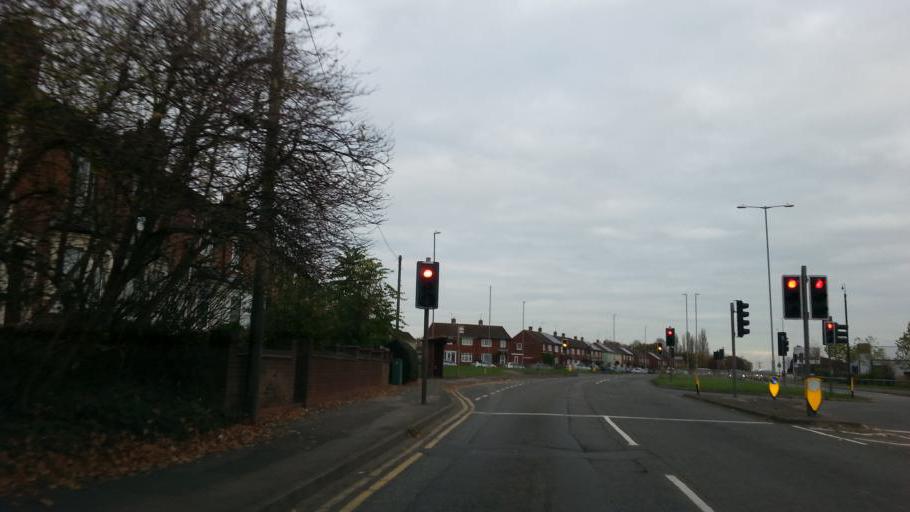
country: GB
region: England
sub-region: Northamptonshire
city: Corby
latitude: 52.4874
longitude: -0.6870
